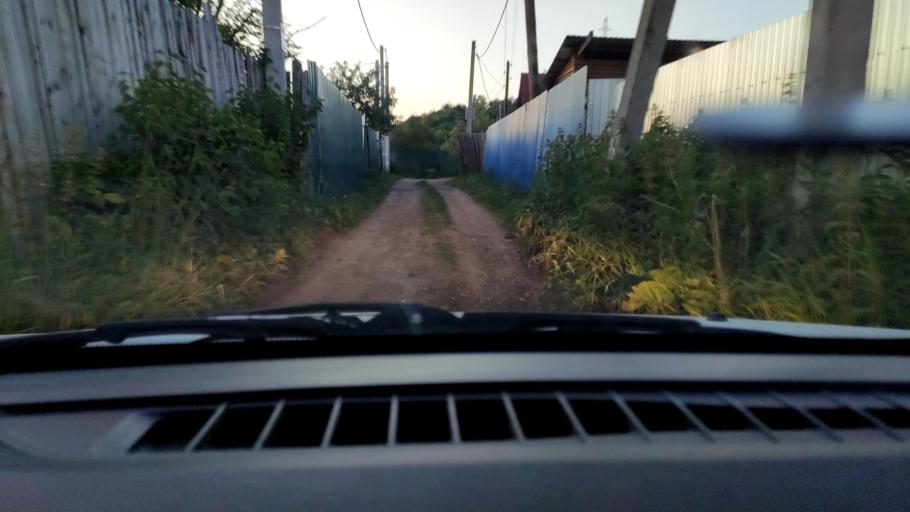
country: RU
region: Perm
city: Kondratovo
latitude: 57.9530
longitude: 56.1455
